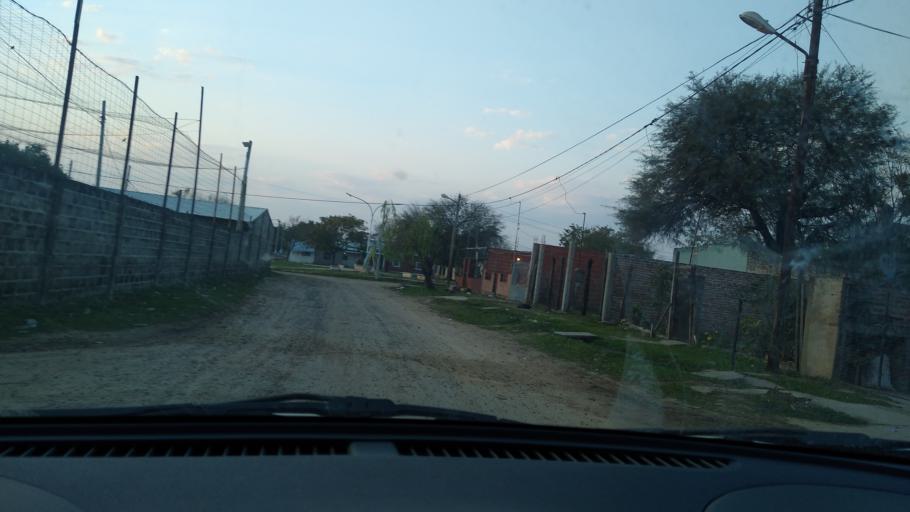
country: AR
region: Chaco
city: Resistencia
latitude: -27.4579
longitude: -58.9635
